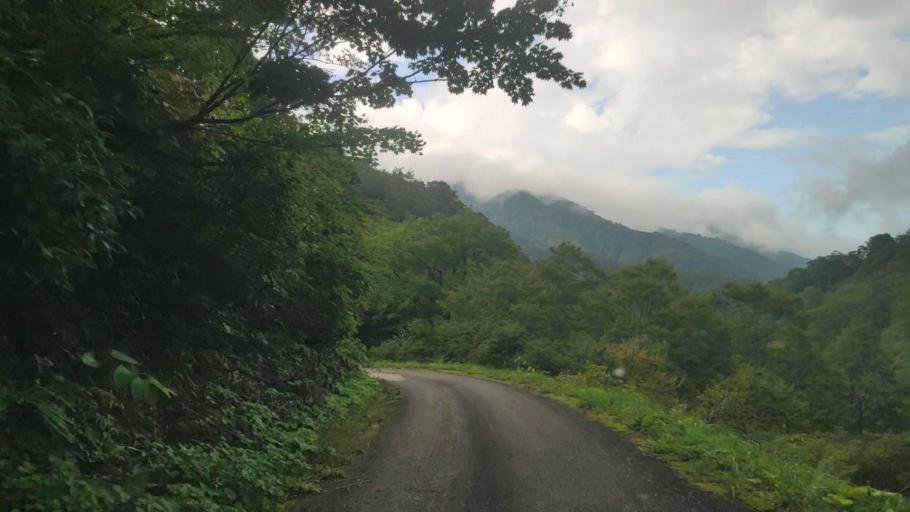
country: JP
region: Toyama
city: Yatsuomachi-higashikumisaka
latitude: 36.3508
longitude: 137.0644
